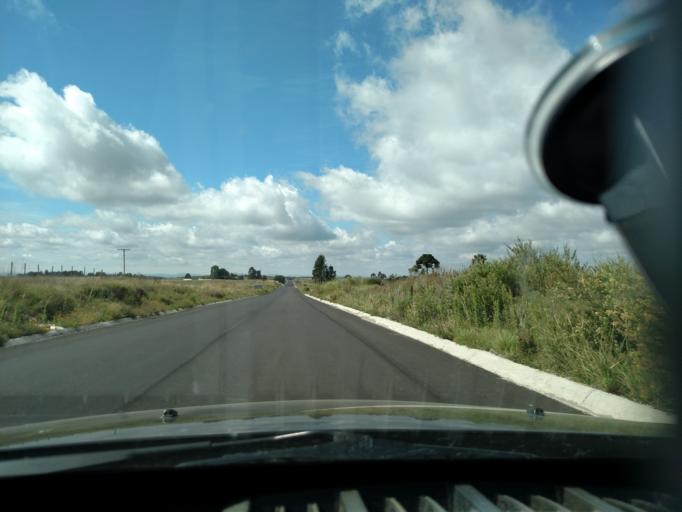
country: BR
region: Santa Catarina
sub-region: Lages
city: Lages
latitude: -27.9797
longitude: -50.0925
